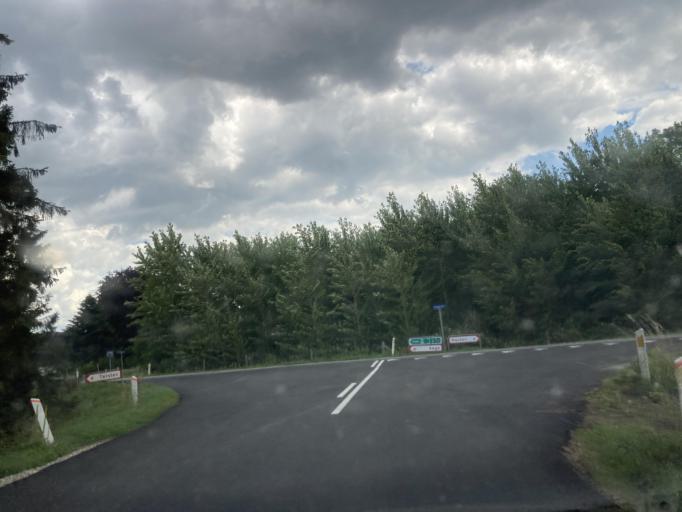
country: DK
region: Zealand
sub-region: Faxe Kommune
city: Haslev
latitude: 55.3279
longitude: 12.0106
